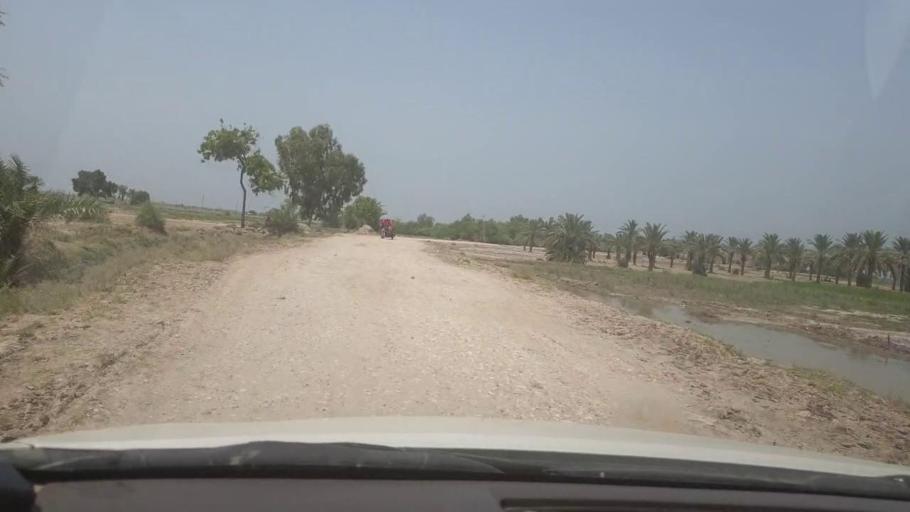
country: PK
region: Sindh
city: Shikarpur
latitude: 27.9451
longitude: 68.5717
